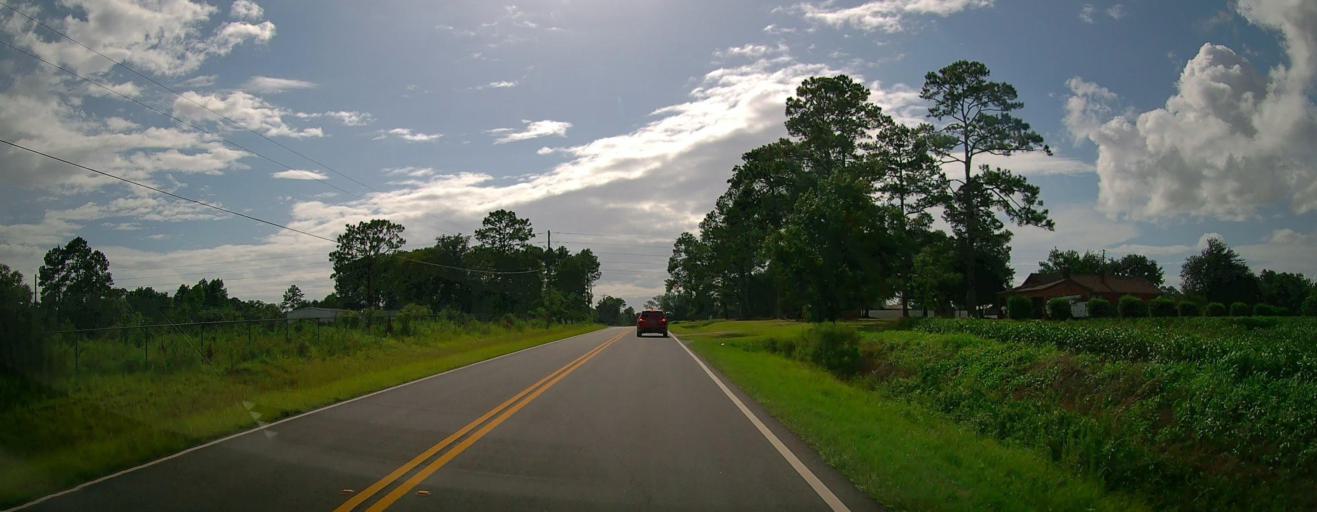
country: US
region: Georgia
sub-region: Coffee County
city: Douglas
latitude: 31.4481
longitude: -82.8710
